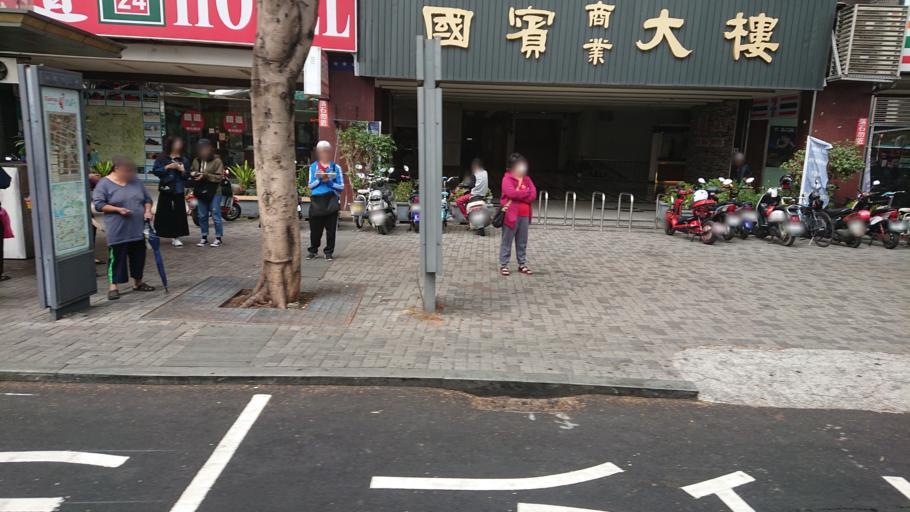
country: TW
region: Taiwan
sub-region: Tainan
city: Tainan
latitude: 22.9977
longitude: 120.2113
